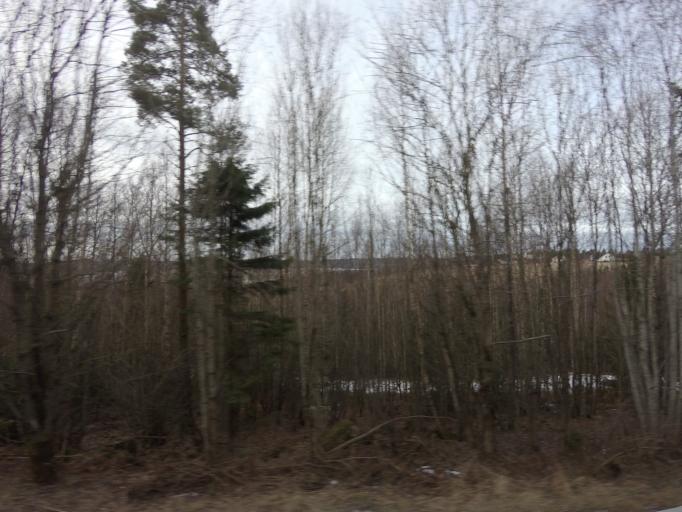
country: NO
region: Akershus
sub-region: Fet
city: Fetsund
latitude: 59.8917
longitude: 11.1993
